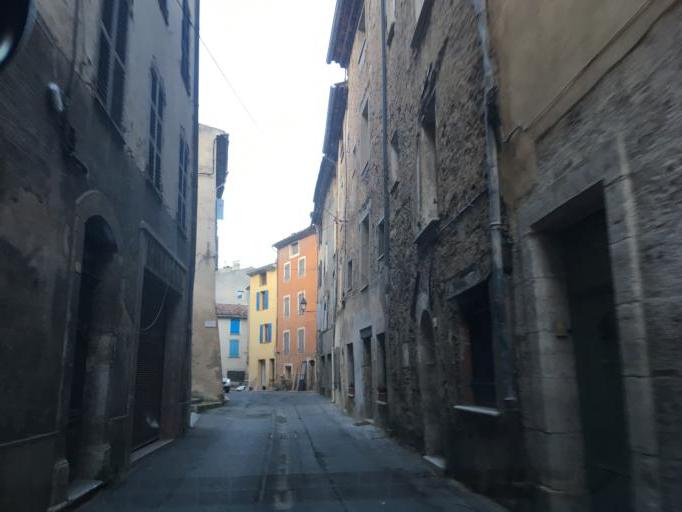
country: FR
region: Provence-Alpes-Cote d'Azur
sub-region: Departement du Var
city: Salernes
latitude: 43.5140
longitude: 6.2430
